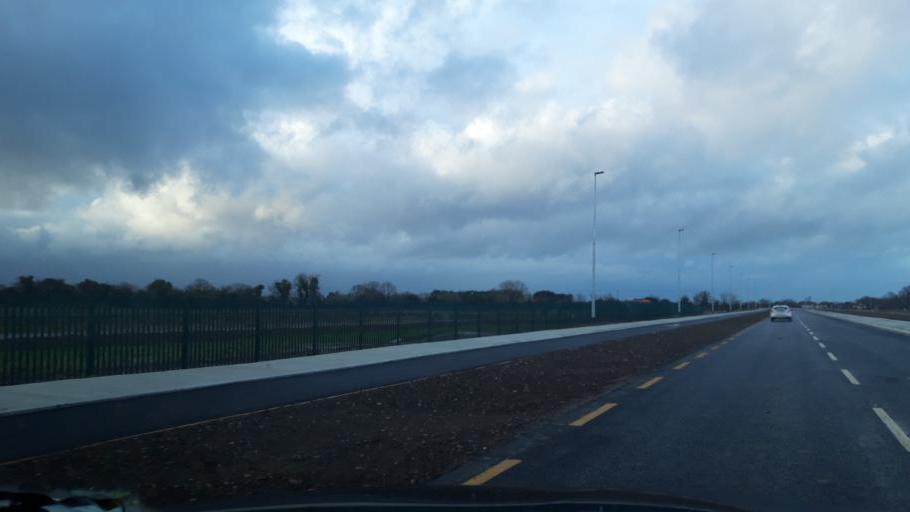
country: IE
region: Leinster
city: Donabate
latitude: 53.4846
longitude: -6.1375
